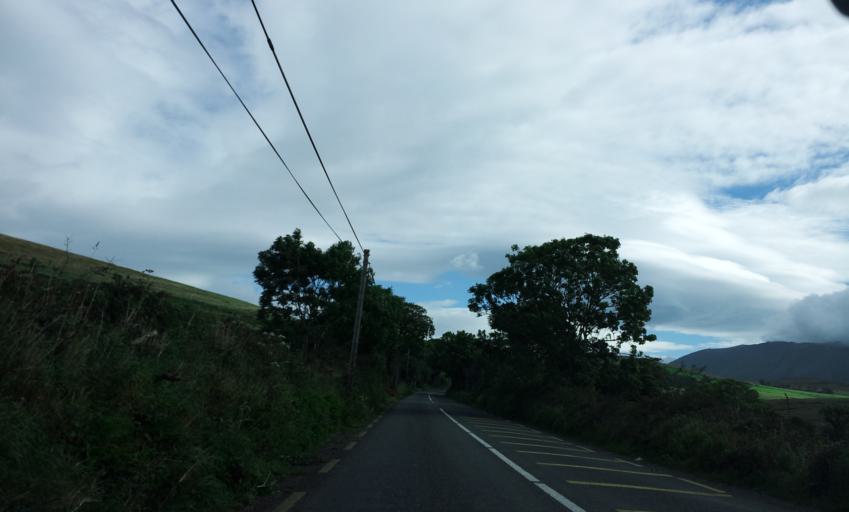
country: IE
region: Munster
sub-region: Ciarrai
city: Killorglin
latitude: 52.1888
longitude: -9.9510
